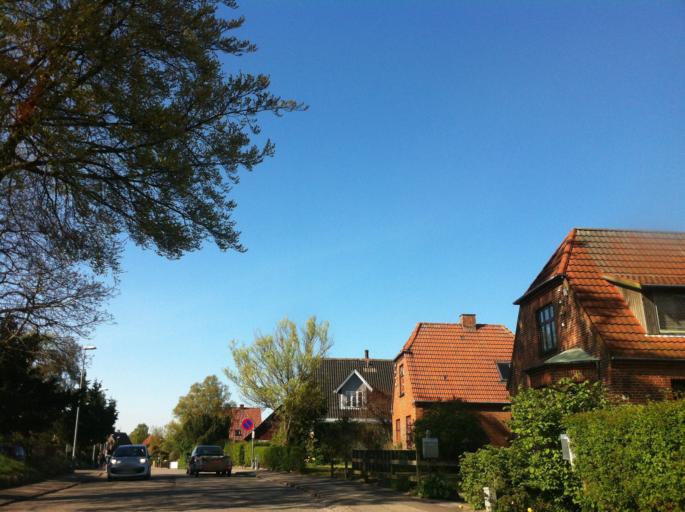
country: DK
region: Zealand
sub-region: Naestved Kommune
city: Naestved
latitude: 55.2374
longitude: 11.7637
